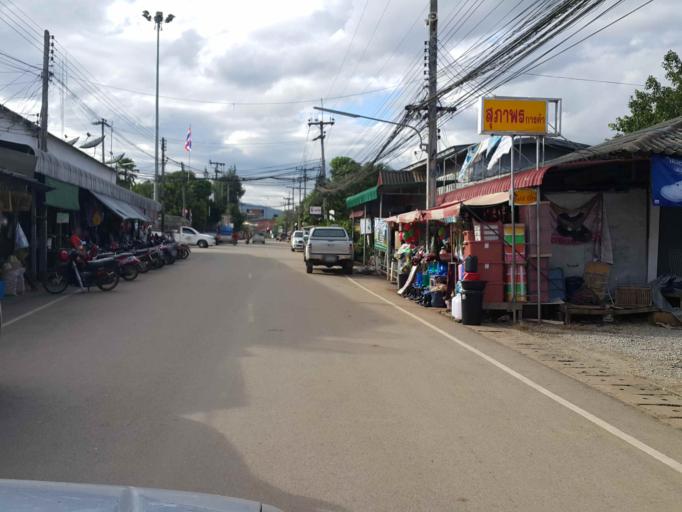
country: TH
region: Chiang Mai
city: Mae Chaem
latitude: 18.4984
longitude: 98.3629
